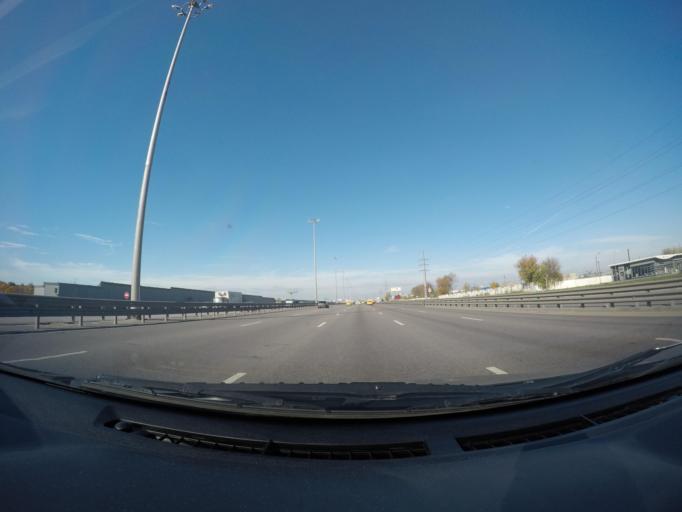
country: RU
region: Moskovskaya
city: Tomilino
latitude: 55.6446
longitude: 37.9150
